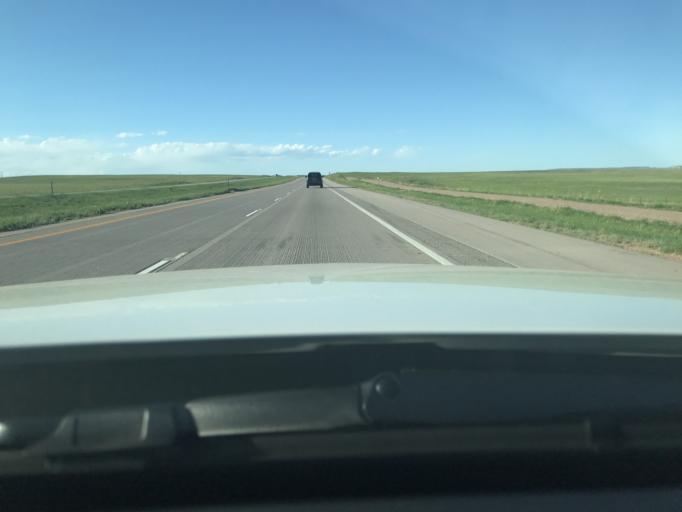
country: US
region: Colorado
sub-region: Larimer County
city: Wellington
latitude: 40.8739
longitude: -104.9552
